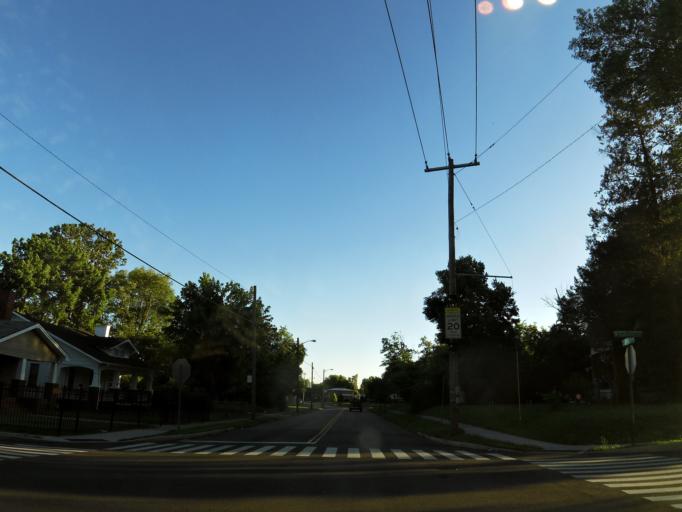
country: US
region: Tennessee
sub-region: Knox County
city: Knoxville
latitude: 35.9927
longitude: -83.8856
